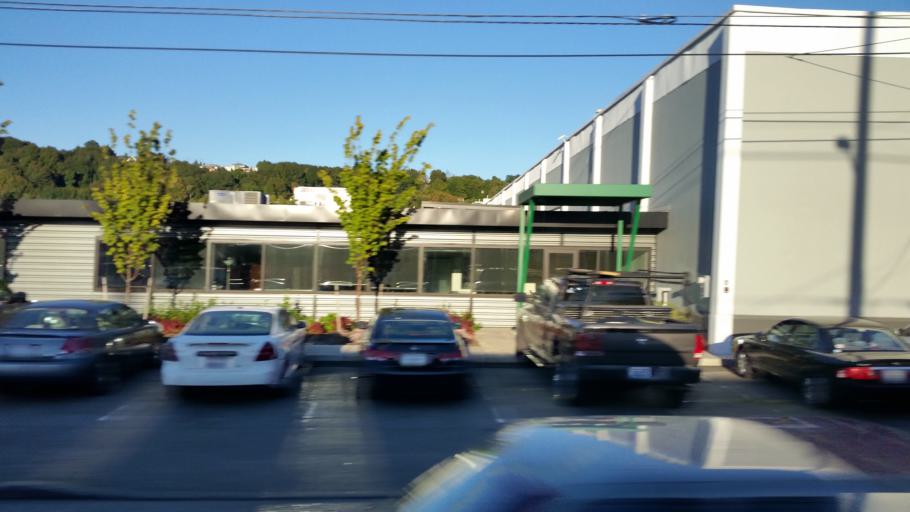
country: US
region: Washington
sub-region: King County
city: Seattle
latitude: 47.5842
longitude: -122.3261
